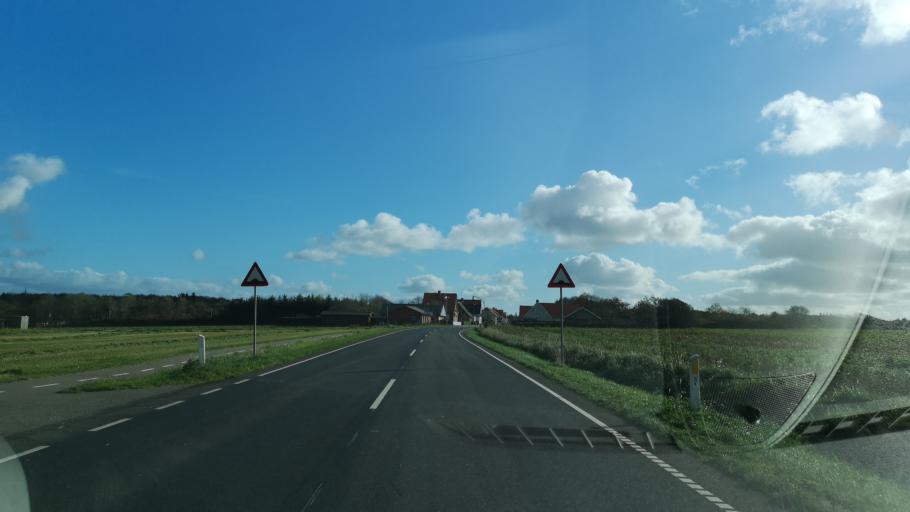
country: DK
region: South Denmark
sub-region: Varde Kommune
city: Oksbol
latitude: 55.7137
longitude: 8.2992
